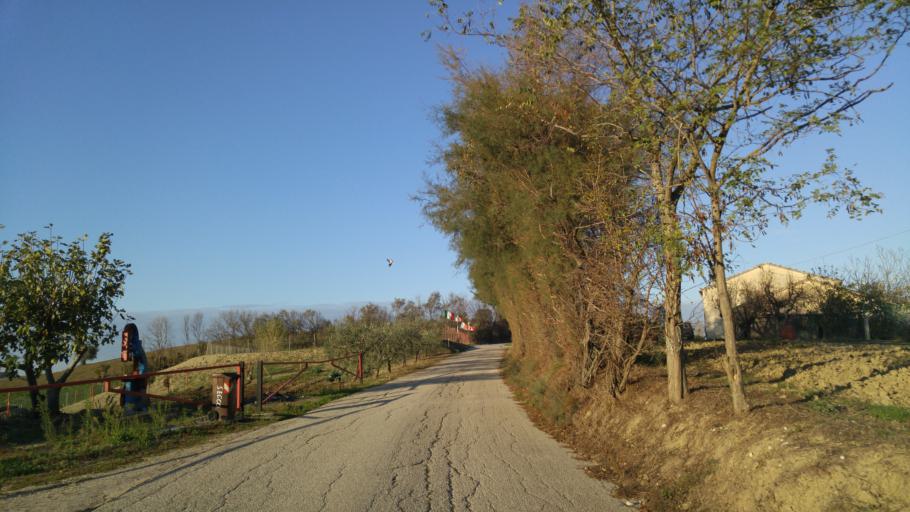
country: IT
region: The Marches
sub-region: Provincia di Pesaro e Urbino
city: Cartoceto
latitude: 43.7908
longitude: 12.8990
